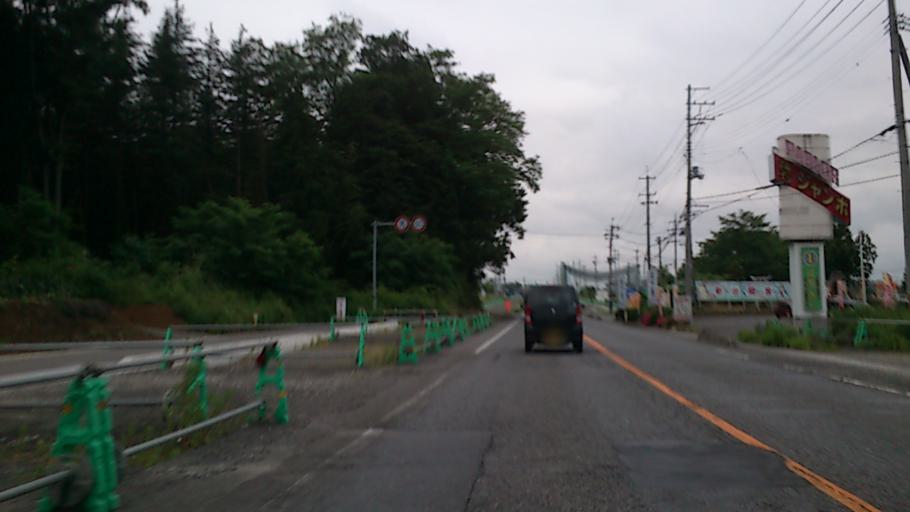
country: JP
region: Fukushima
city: Sukagawa
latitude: 37.2676
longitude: 140.3550
